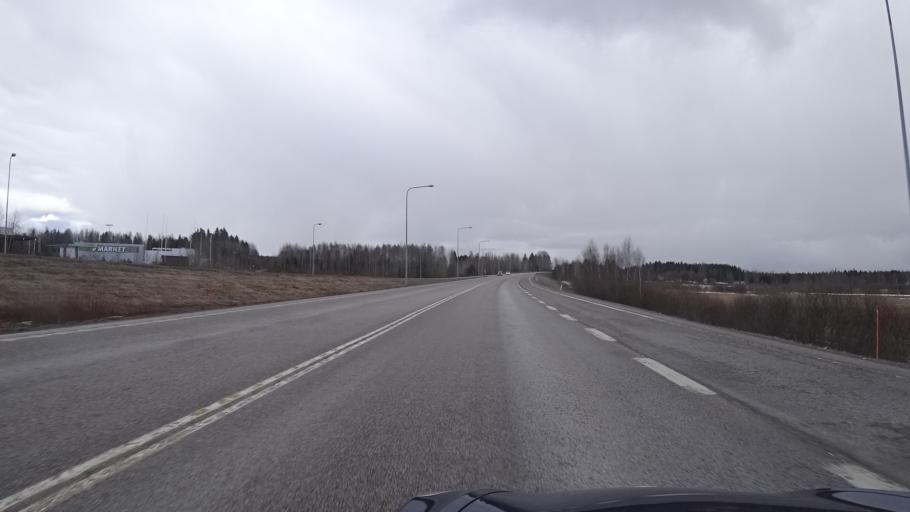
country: FI
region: Paijanne Tavastia
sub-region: Lahti
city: Nastola
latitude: 60.9453
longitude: 25.8868
